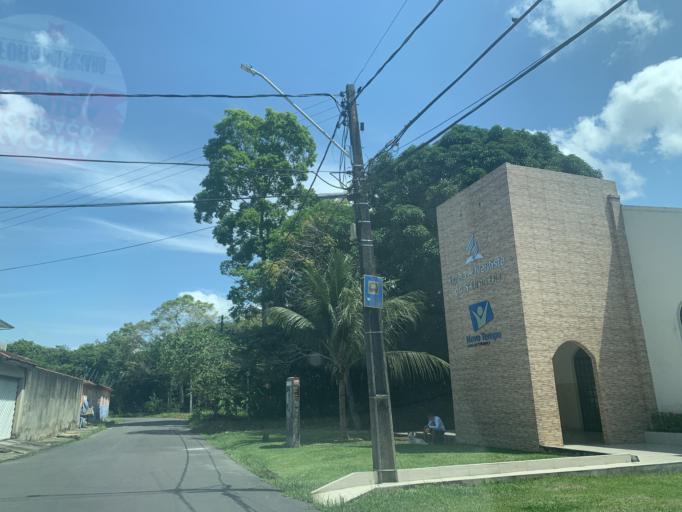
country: BR
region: Amazonas
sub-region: Manaus
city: Manaus
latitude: -3.1018
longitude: -59.9653
